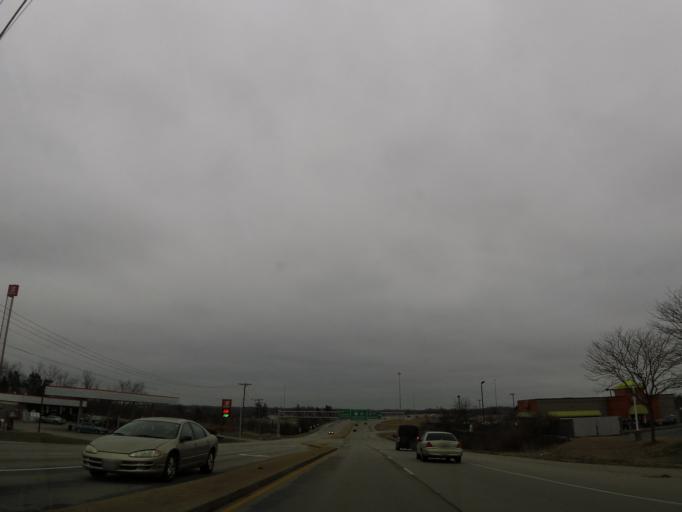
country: US
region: Kentucky
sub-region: Franklin County
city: Frankfort
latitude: 38.1639
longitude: -84.8965
